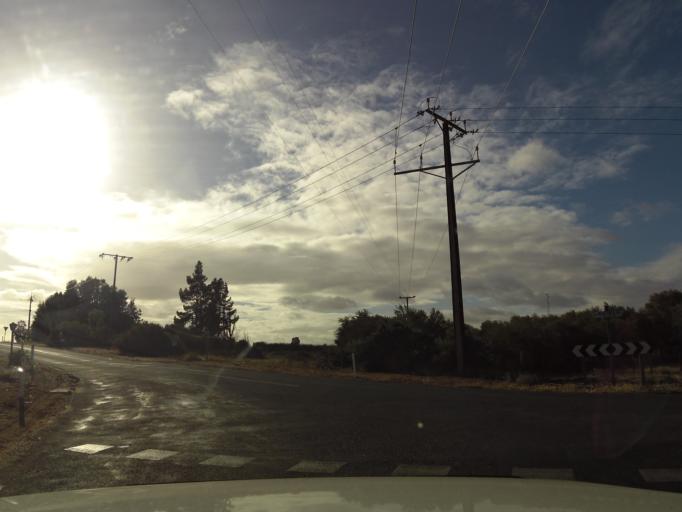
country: AU
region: South Australia
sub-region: Berri and Barmera
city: Berri
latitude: -34.2711
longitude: 140.5877
